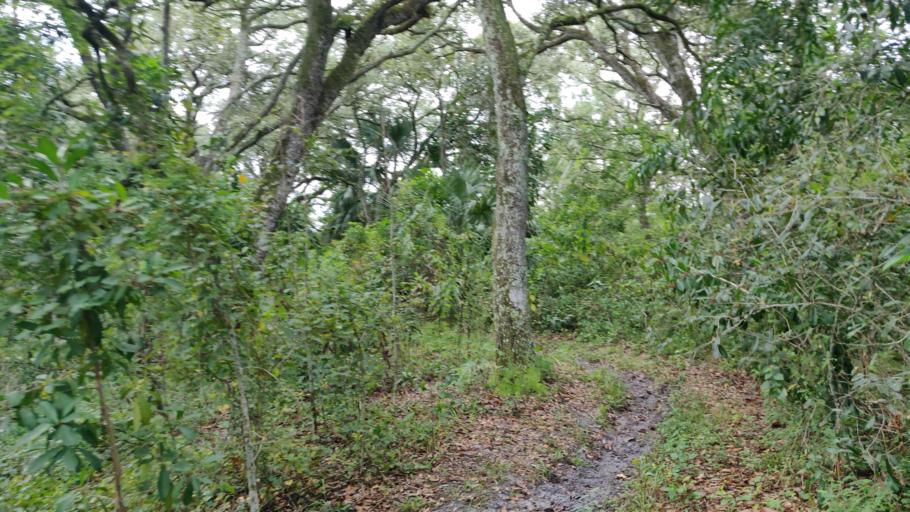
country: US
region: Florida
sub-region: Broward County
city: Cooper City
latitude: 26.0740
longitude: -80.2726
